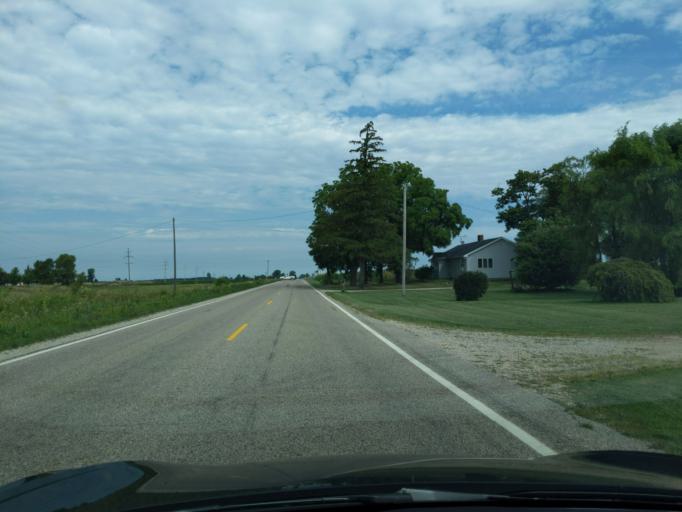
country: US
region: Michigan
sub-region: Gratiot County
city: Breckenridge
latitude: 43.3192
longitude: -84.4293
